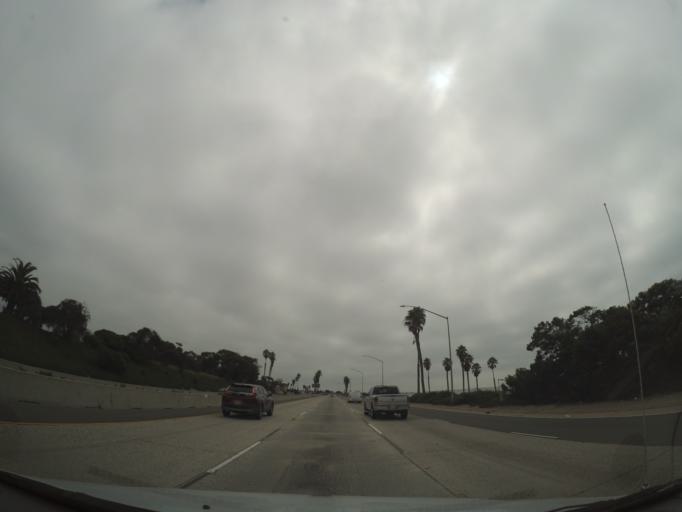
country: US
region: California
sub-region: Ventura County
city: Ventura
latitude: 34.2747
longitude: -119.2867
